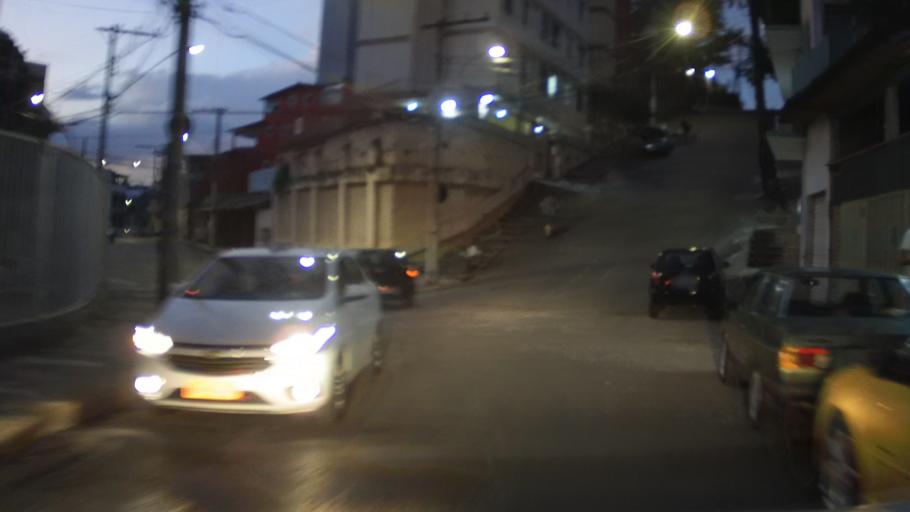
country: BR
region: Minas Gerais
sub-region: Belo Horizonte
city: Belo Horizonte
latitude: -19.8959
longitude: -43.9345
